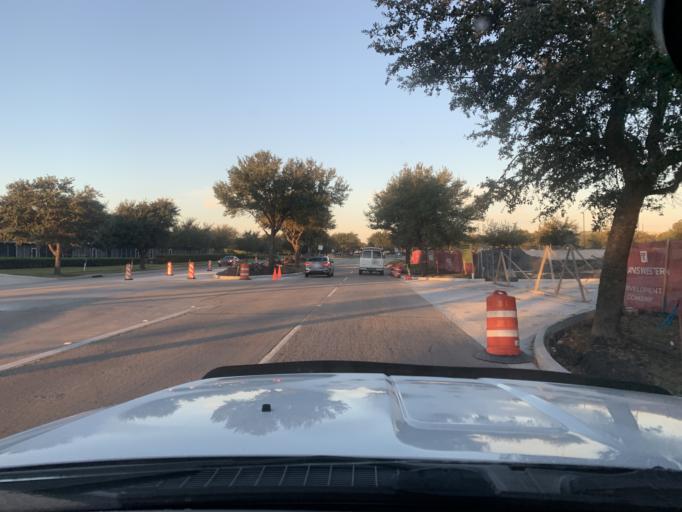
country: US
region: Texas
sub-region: Fort Bend County
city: Meadows Place
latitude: 29.6479
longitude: -95.5998
